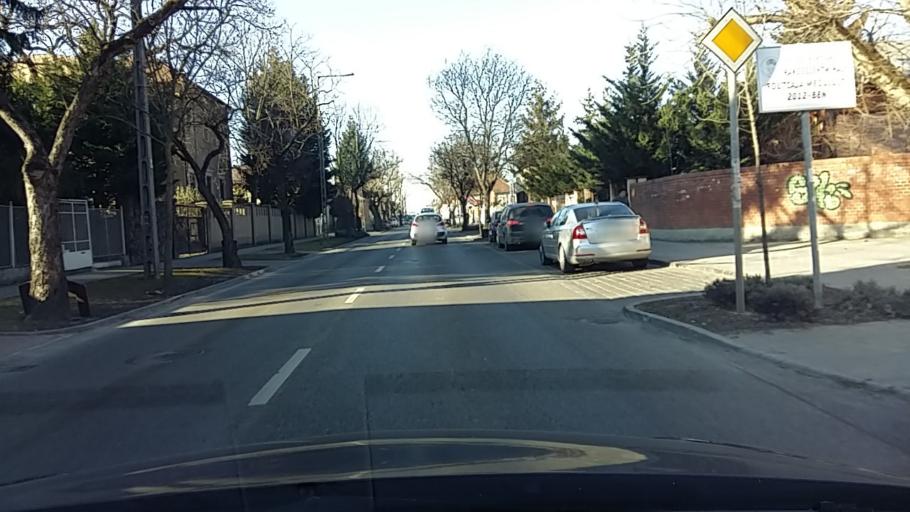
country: HU
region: Budapest
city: Budapest XVI. keruelet
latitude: 47.5224
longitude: 19.1700
